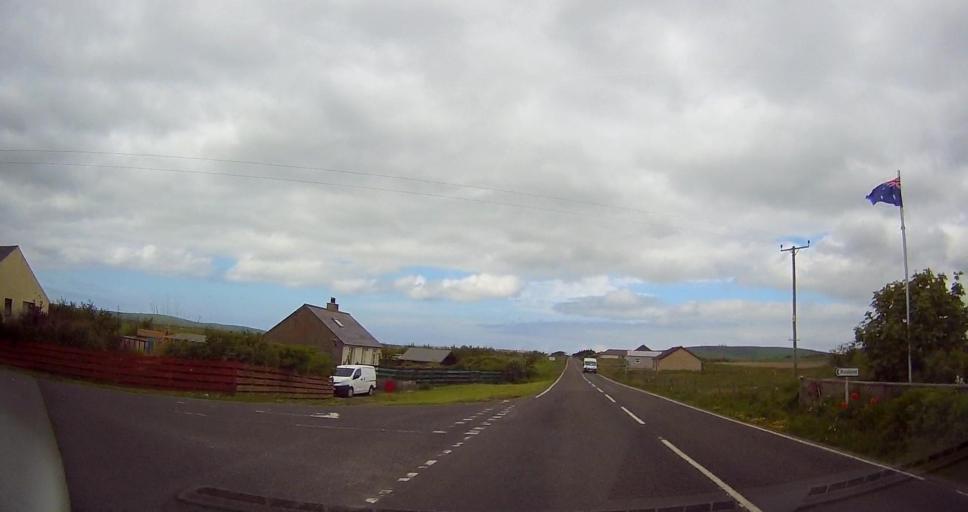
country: GB
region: Scotland
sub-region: Orkney Islands
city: Stromness
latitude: 59.0557
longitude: -3.2160
